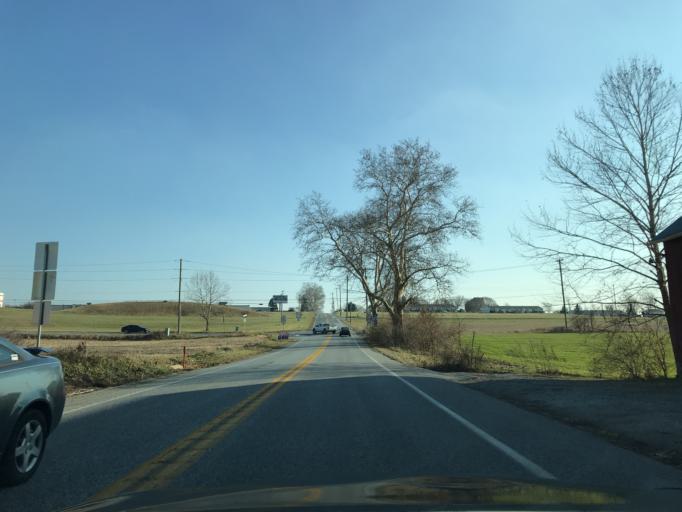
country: US
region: Pennsylvania
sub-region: York County
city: Loganville
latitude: 39.8239
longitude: -76.6977
